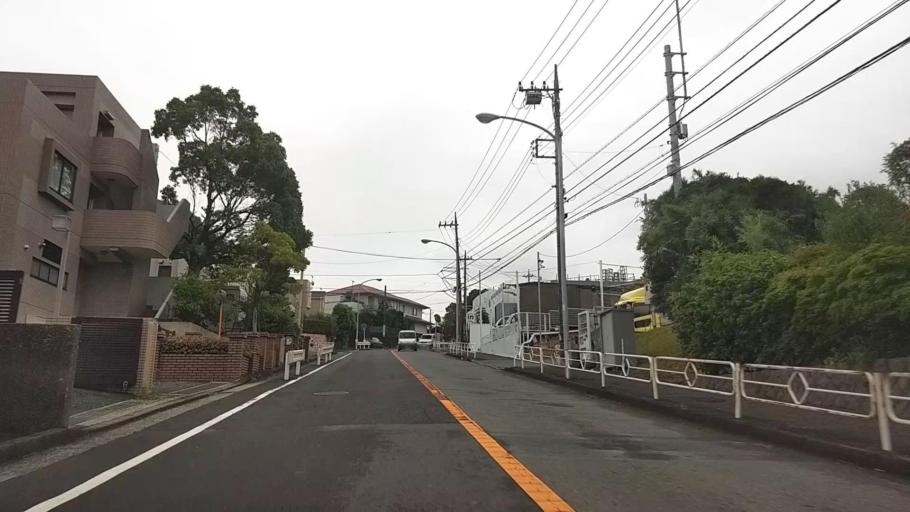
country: JP
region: Kanagawa
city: Yokohama
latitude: 35.3900
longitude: 139.5796
